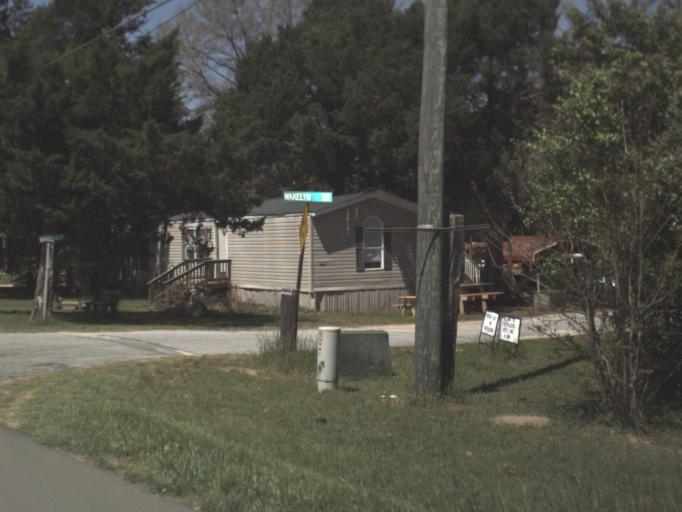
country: US
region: Florida
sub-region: Walton County
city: DeFuniak Springs
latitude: 30.7275
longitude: -86.0852
